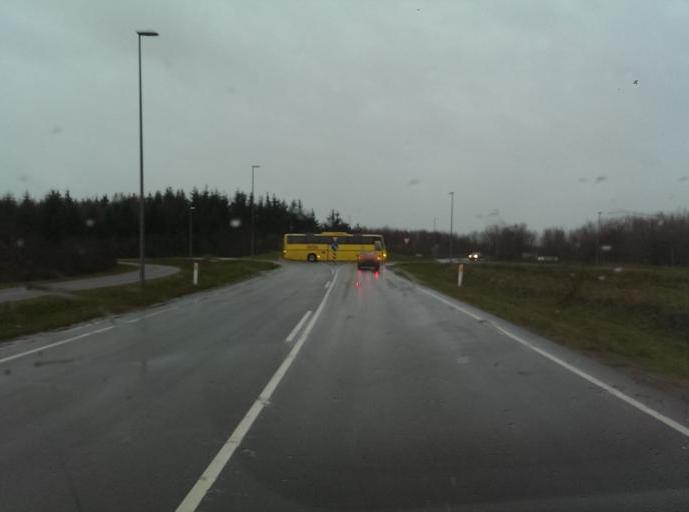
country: DK
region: South Denmark
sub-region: Esbjerg Kommune
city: Esbjerg
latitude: 55.4855
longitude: 8.5082
